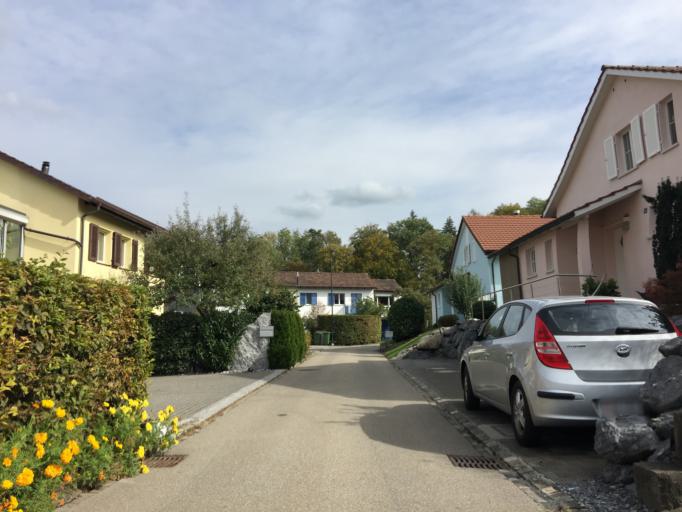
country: CH
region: Saint Gallen
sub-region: Wahlkreis Wil
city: Oberuzwil
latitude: 47.4327
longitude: 9.1336
